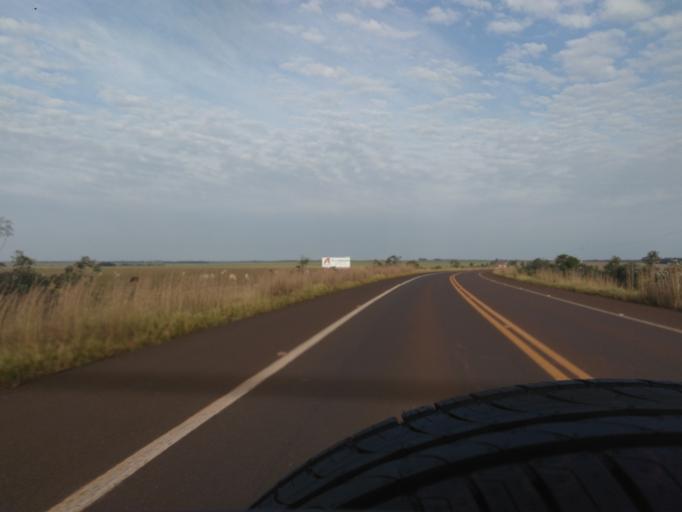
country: BR
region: Mato Grosso do Sul
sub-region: Ponta Pora
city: Ponta Pora
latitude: -22.5904
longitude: -55.5209
